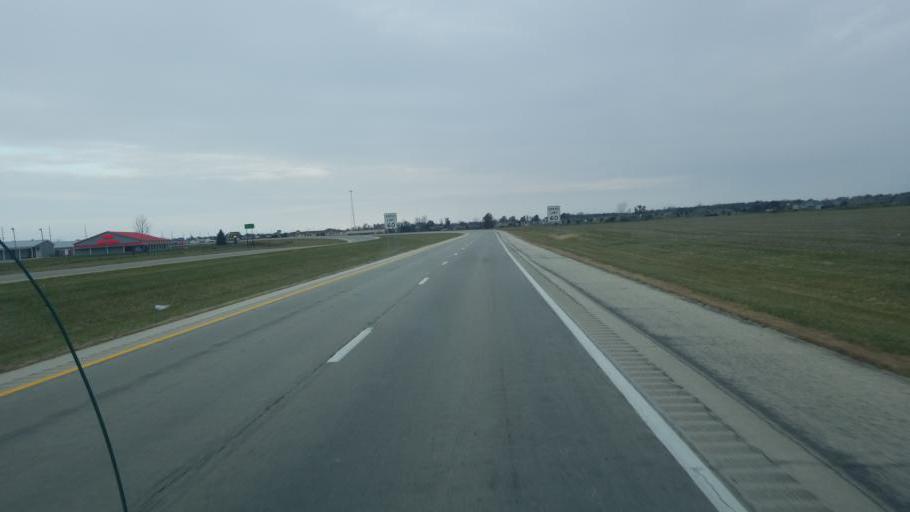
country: US
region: Ohio
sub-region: Mercer County
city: Celina
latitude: 40.5586
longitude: -84.5268
